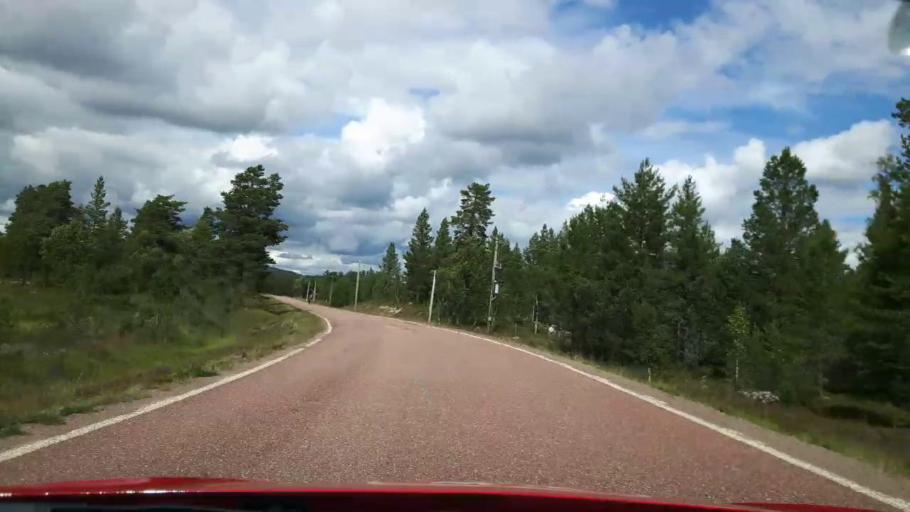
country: NO
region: Hedmark
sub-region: Trysil
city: Innbygda
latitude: 62.0924
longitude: 12.9743
